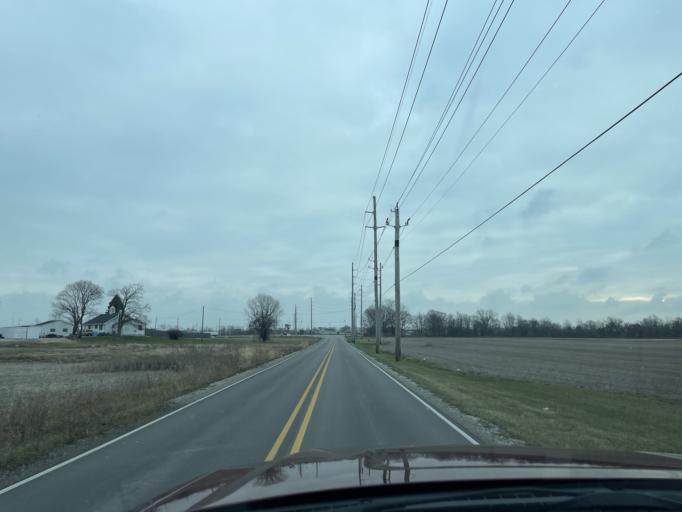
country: US
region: Indiana
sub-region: Boone County
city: Whitestown
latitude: 39.9459
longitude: -86.3630
